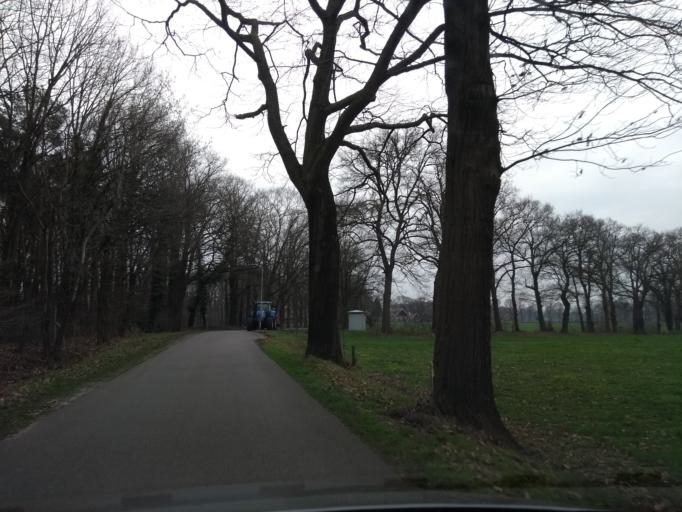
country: NL
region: Overijssel
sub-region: Gemeente Enschede
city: Enschede
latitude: 52.1759
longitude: 6.8935
